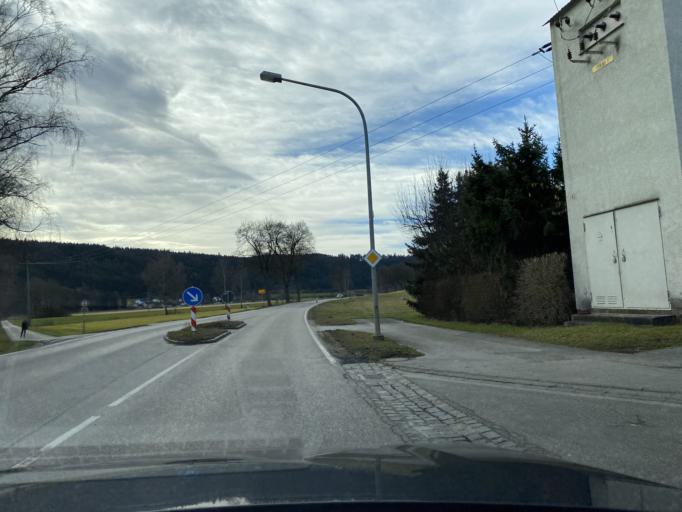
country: DE
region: Bavaria
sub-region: Upper Palatinate
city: Dietfurt
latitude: 49.0176
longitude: 11.5578
